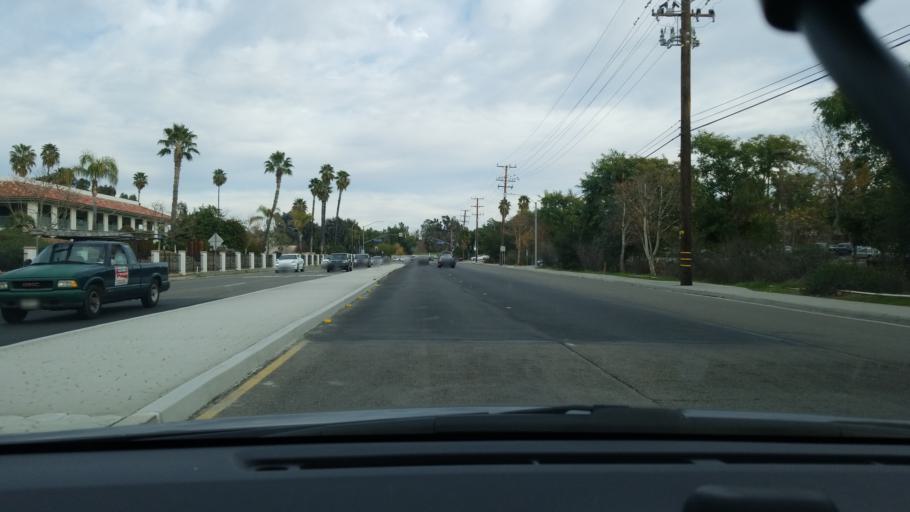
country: US
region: California
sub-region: Riverside County
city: Murrieta Hot Springs
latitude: 33.5562
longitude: -117.1557
